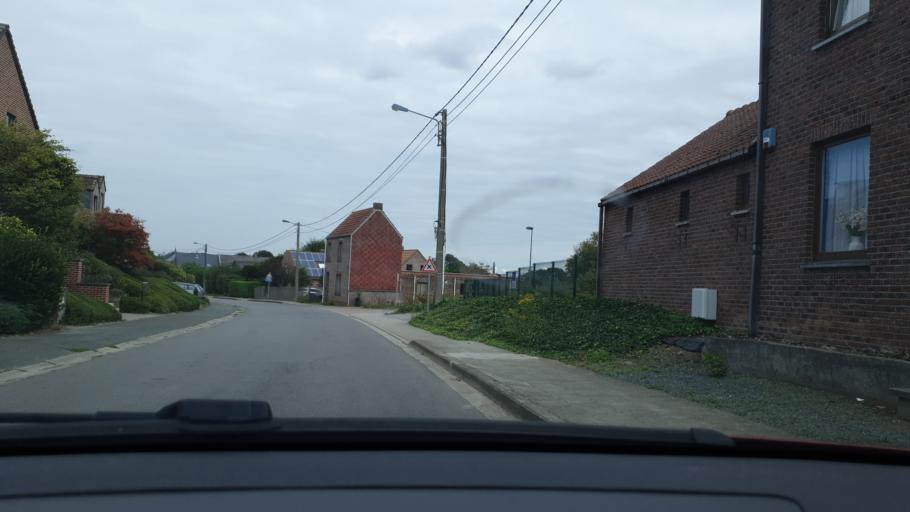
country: BE
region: Wallonia
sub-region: Province du Brabant Wallon
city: Rebecq-Rognon
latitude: 50.6848
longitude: 4.0787
